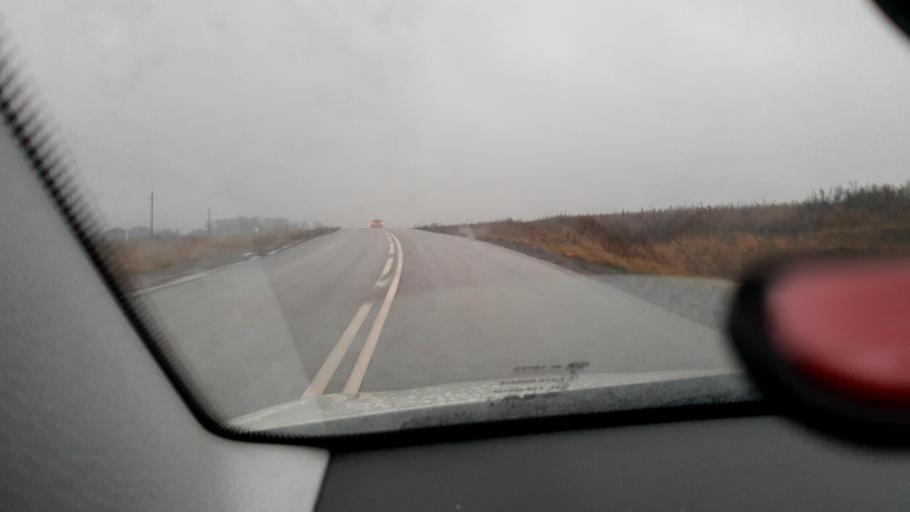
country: RU
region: Bashkortostan
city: Blagoveshchensk
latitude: 54.9013
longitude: 56.1769
